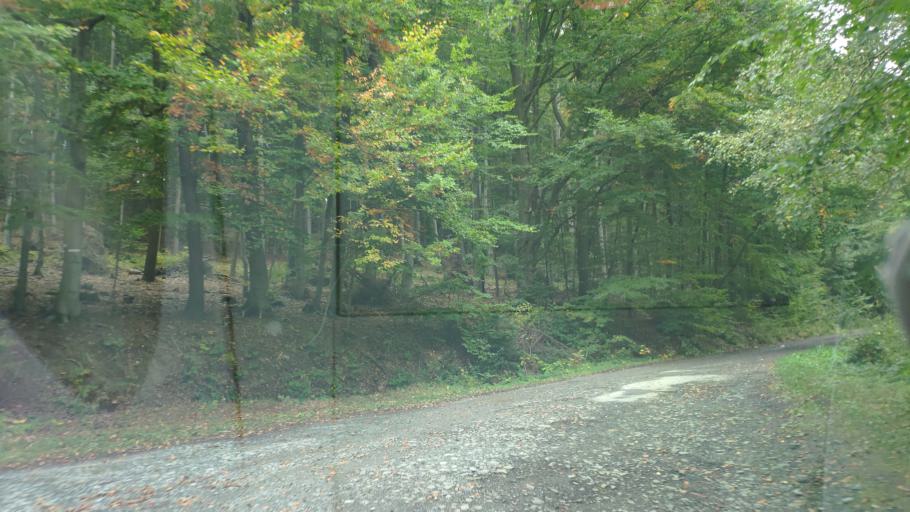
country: SK
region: Presovsky
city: Giraltovce
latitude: 48.9103
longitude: 21.4616
